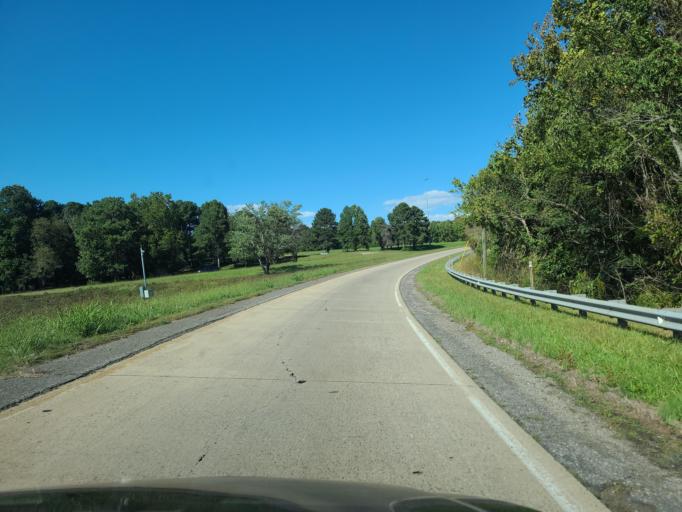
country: US
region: North Carolina
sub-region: Catawba County
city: Mountain View
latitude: 35.7057
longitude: -81.3514
